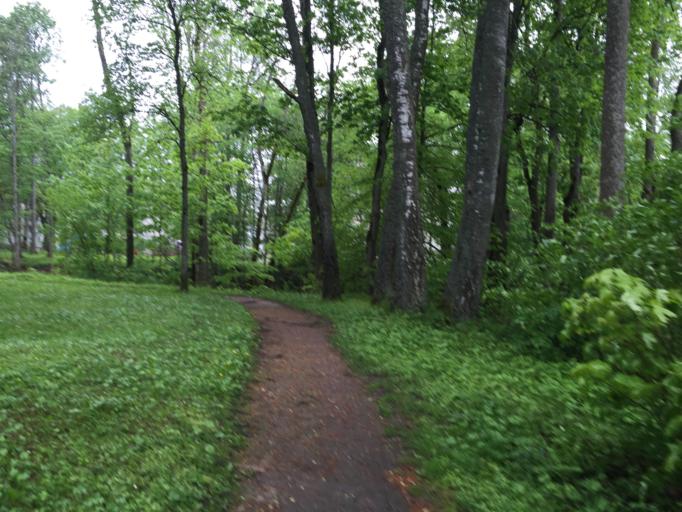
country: LV
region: Lielvarde
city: Lielvarde
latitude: 56.7123
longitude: 24.8379
